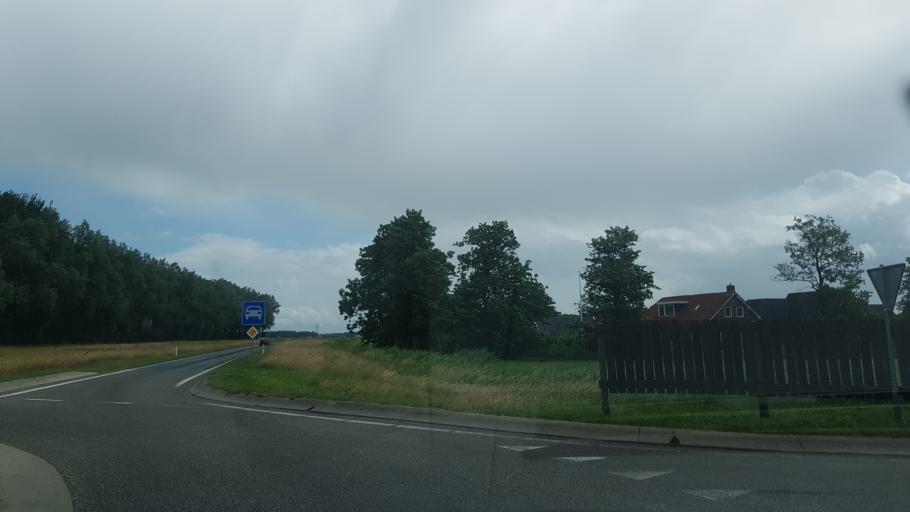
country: NL
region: Friesland
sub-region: Gemeente Dantumadiel
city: Rinsumageast
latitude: 53.3005
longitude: 5.9461
